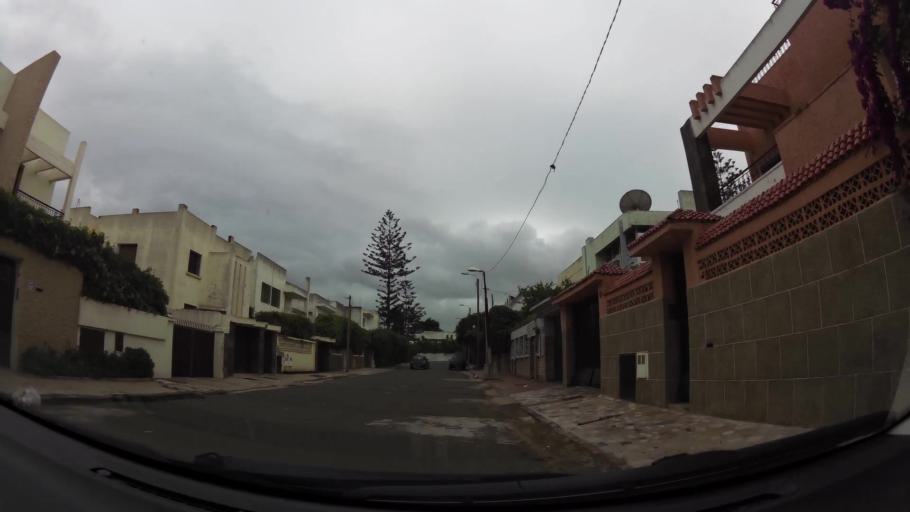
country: MA
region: Grand Casablanca
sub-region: Casablanca
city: Casablanca
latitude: 33.5942
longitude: -7.6475
